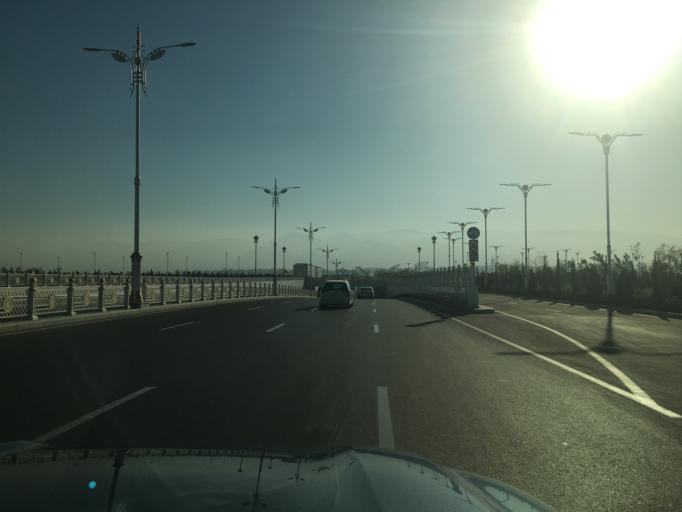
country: TM
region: Ahal
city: Ashgabat
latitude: 37.9728
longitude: 58.3895
